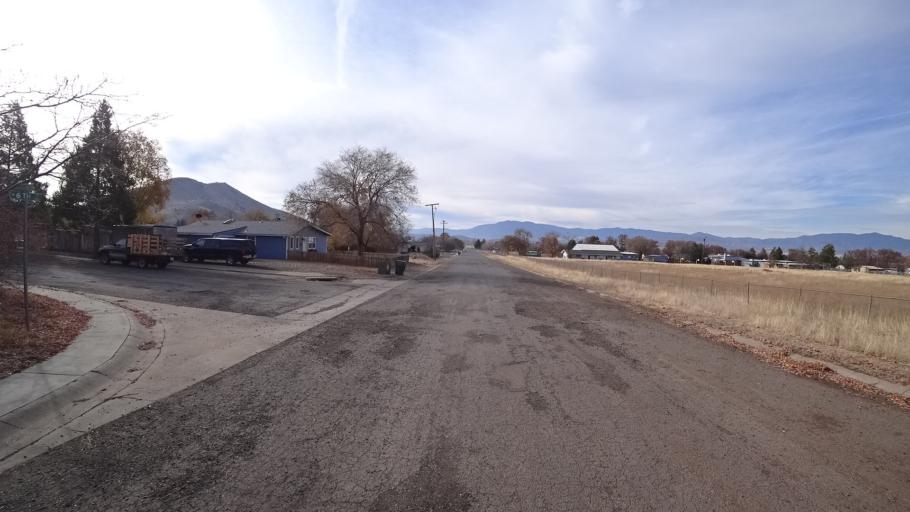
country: US
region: California
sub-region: Siskiyou County
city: Montague
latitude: 41.7287
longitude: -122.5184
